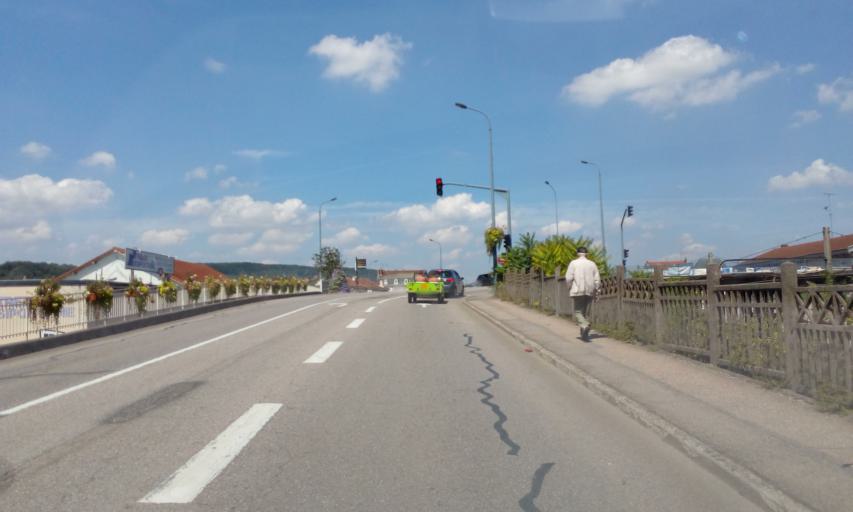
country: FR
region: Lorraine
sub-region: Departement de Meurthe-et-Moselle
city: Maidieres
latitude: 48.8994
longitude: 6.0508
